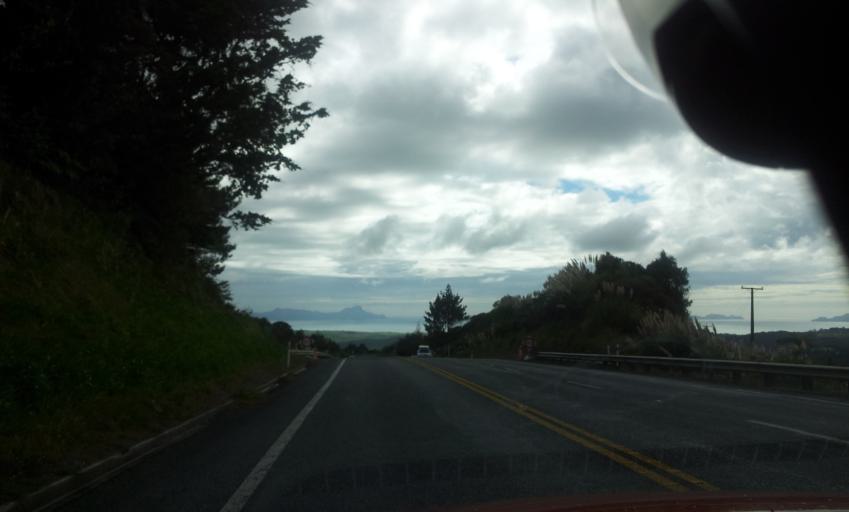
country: NZ
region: Northland
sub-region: Whangarei
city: Ruakaka
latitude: -36.0667
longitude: 174.4229
